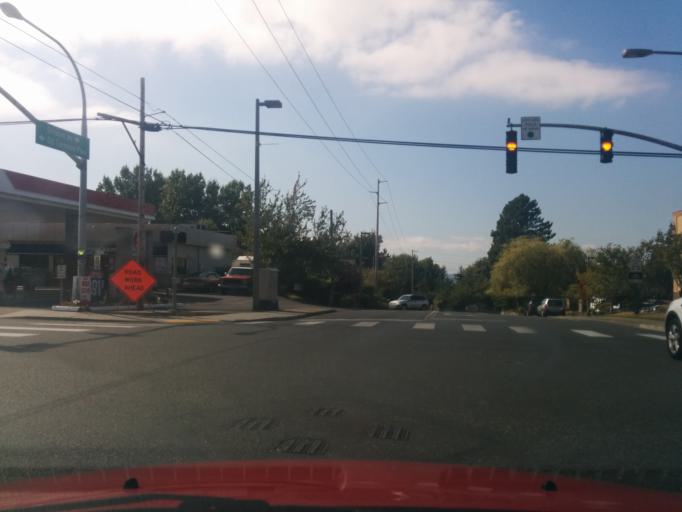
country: US
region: Washington
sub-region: Whatcom County
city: Bellingham
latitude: 48.7176
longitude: -122.5022
